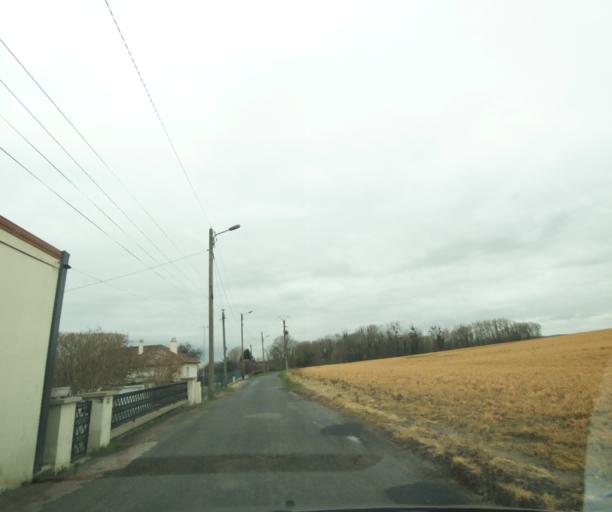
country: FR
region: Picardie
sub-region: Departement de l'Oise
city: Noyon
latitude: 49.5938
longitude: 3.0115
